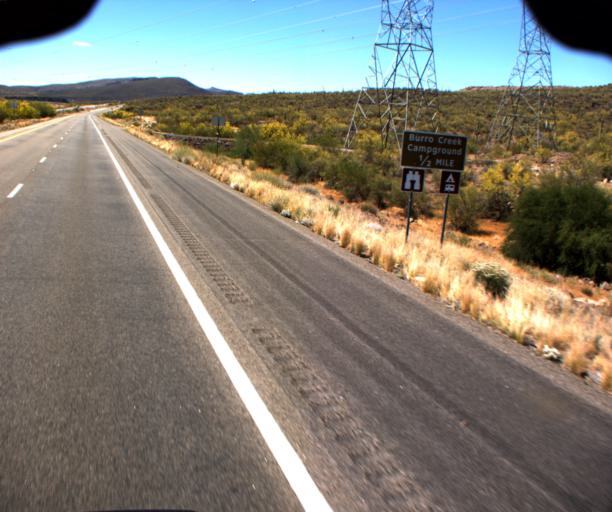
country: US
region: Arizona
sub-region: Yavapai County
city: Bagdad
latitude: 34.5272
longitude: -113.4277
